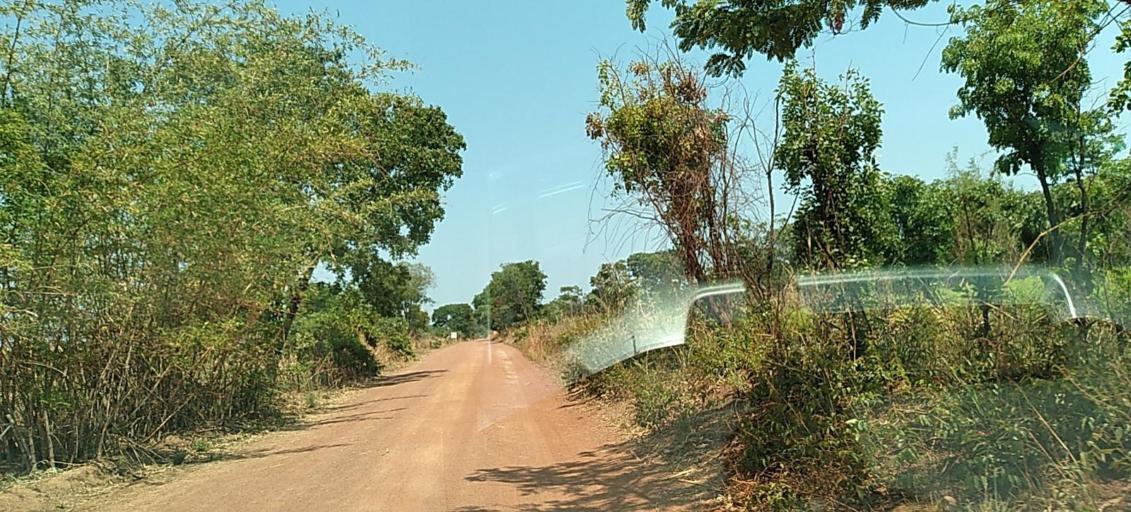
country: ZM
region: Copperbelt
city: Chingola
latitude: -12.5423
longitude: 27.7401
